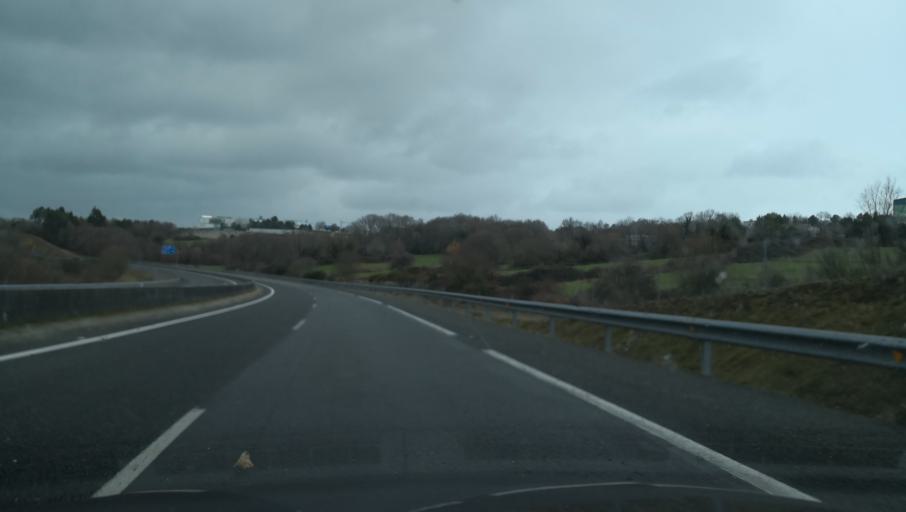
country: ES
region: Galicia
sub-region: Provincia de Pontevedra
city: Lalin
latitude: 42.6663
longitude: -8.1475
